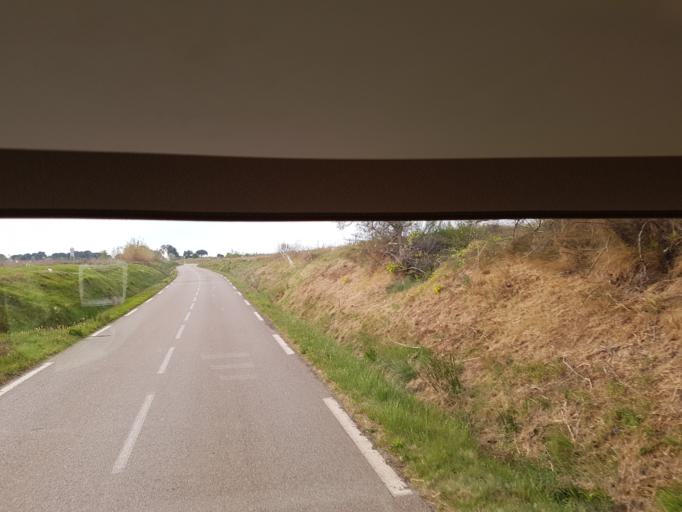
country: FR
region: Languedoc-Roussillon
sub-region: Departement de l'Herault
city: Marseillan
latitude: 43.3665
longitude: 3.5117
